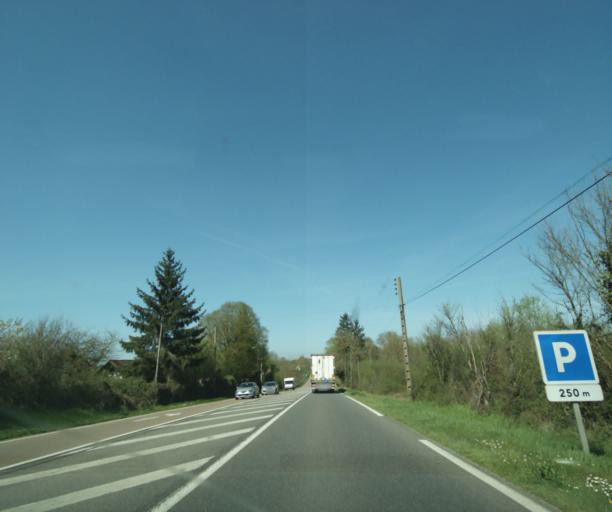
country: FR
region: Bourgogne
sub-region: Departement de la Nievre
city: Chantenay-Saint-Imbert
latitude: 46.7422
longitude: 3.1573
